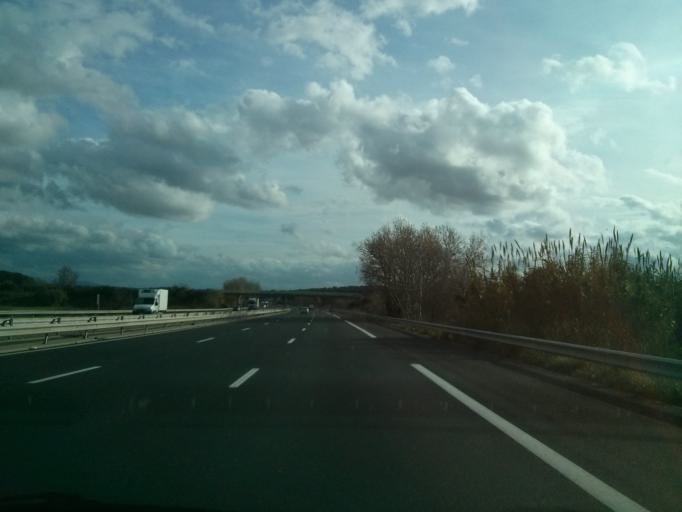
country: FR
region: Provence-Alpes-Cote d'Azur
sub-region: Departement des Bouches-du-Rhone
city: Eguilles
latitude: 43.5410
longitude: 5.3392
